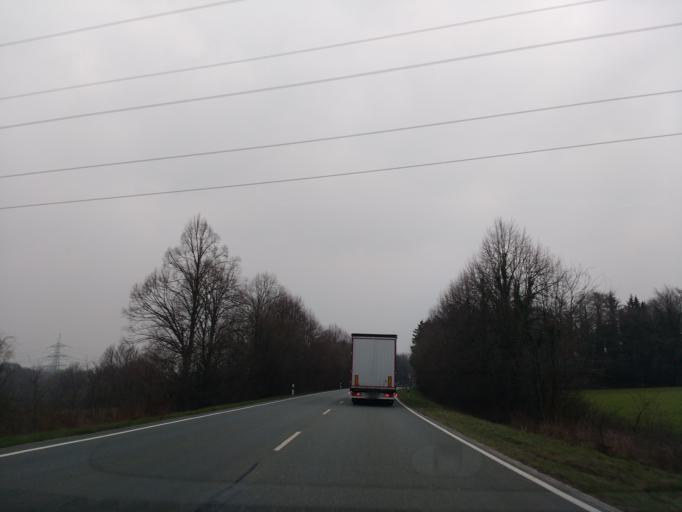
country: DE
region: North Rhine-Westphalia
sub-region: Regierungsbezirk Munster
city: Lotte
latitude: 52.2736
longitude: 7.8950
